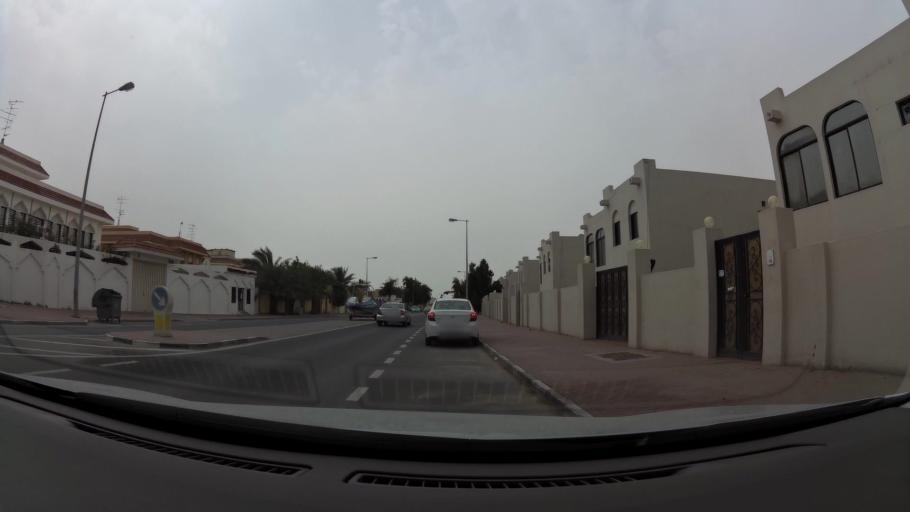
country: QA
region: Baladiyat ad Dawhah
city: Doha
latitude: 25.2522
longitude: 51.5436
